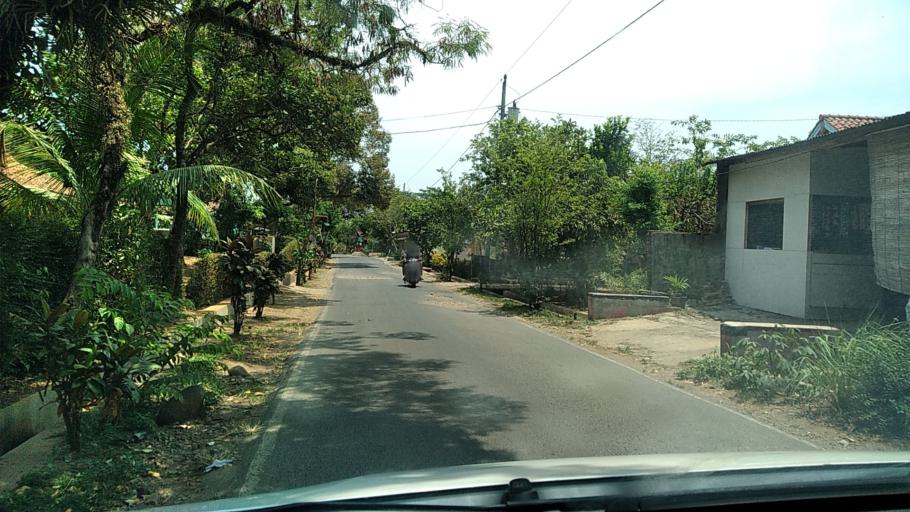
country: ID
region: Central Java
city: Ungaran
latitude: -7.0965
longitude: 110.3186
